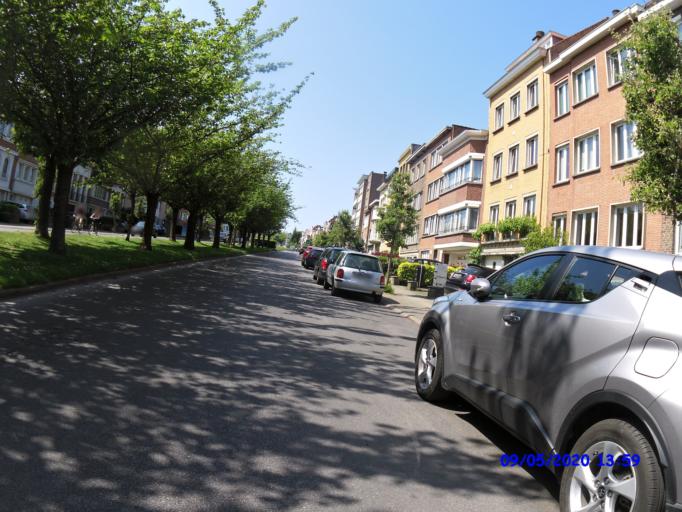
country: BE
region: Flanders
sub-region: Provincie Vlaams-Brabant
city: Kraainem
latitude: 50.8485
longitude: 4.4214
